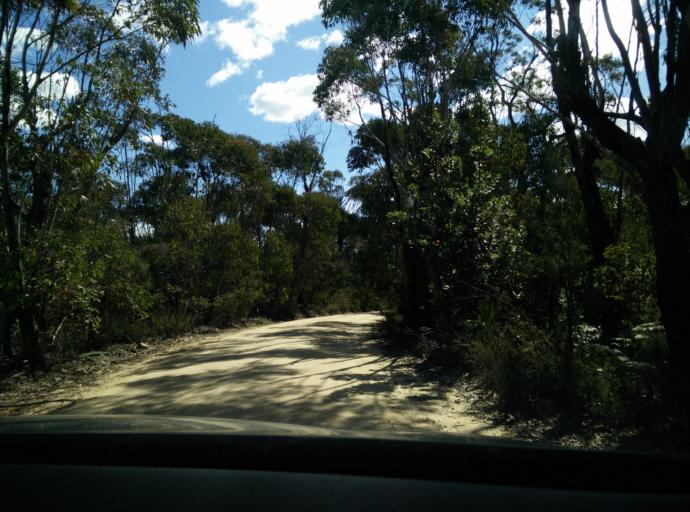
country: AU
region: New South Wales
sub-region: Blue Mountains Municipality
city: Blackheath
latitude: -33.5736
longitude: 150.2904
